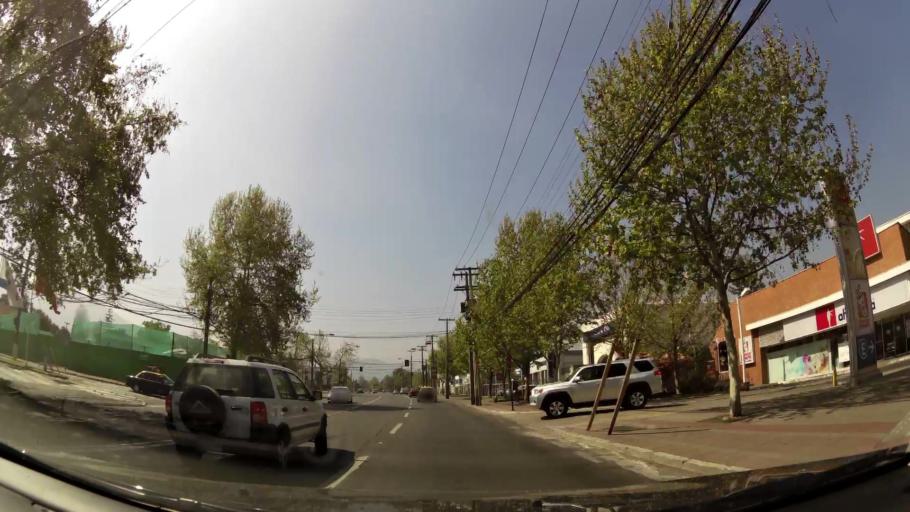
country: CL
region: Santiago Metropolitan
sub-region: Provincia de Santiago
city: Villa Presidente Frei, Nunoa, Santiago, Chile
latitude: -33.3900
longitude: -70.5703
